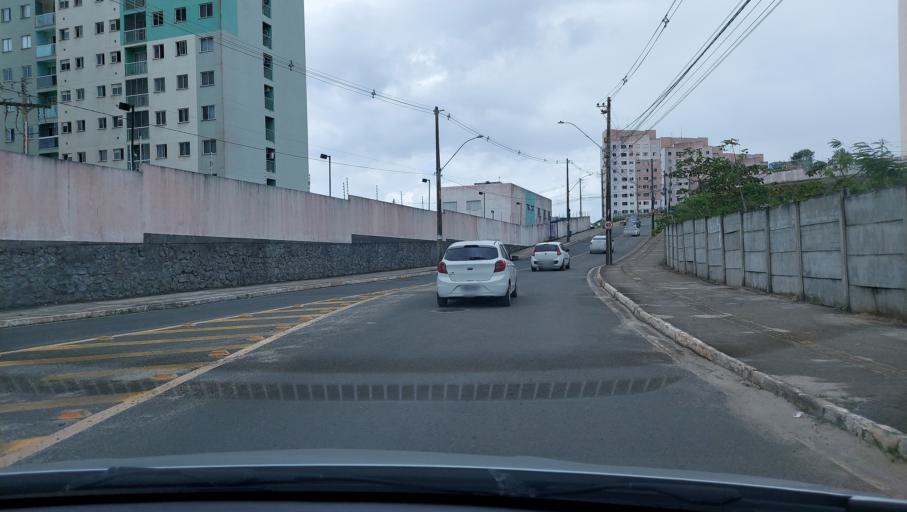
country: BR
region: Bahia
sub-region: Lauro De Freitas
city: Lauro de Freitas
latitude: -12.9379
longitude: -38.3790
